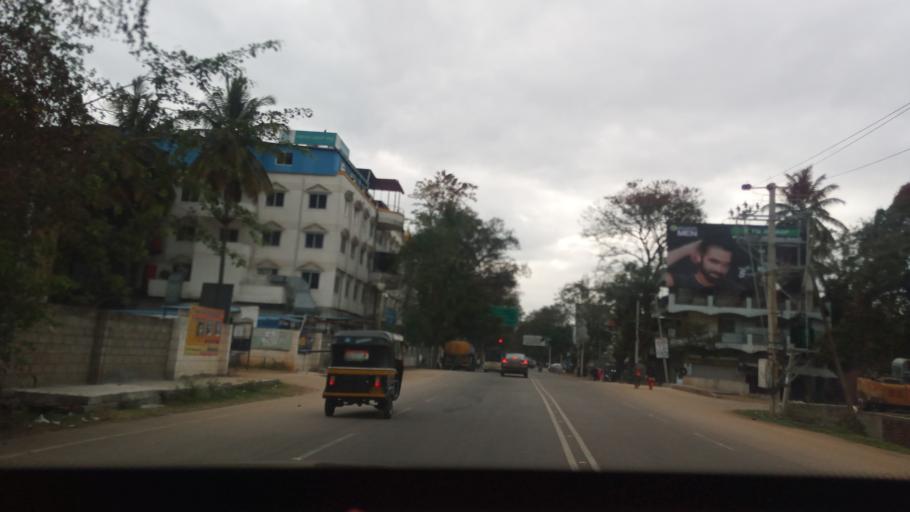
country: IN
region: Karnataka
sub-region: Mysore
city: Mysore
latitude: 12.2963
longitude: 76.6334
